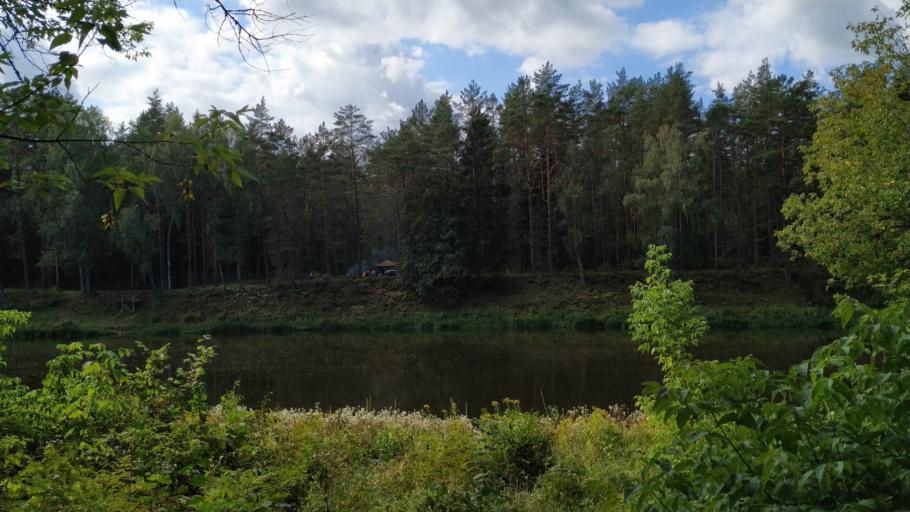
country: LT
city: Grigiskes
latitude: 54.8049
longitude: 24.9728
